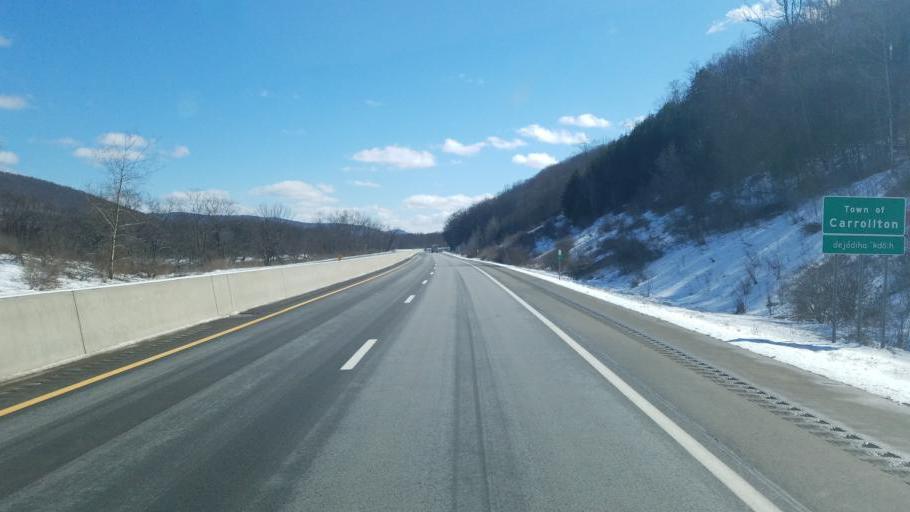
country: US
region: New York
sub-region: Cattaraugus County
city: Salamanca
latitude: 42.1244
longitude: -78.6659
